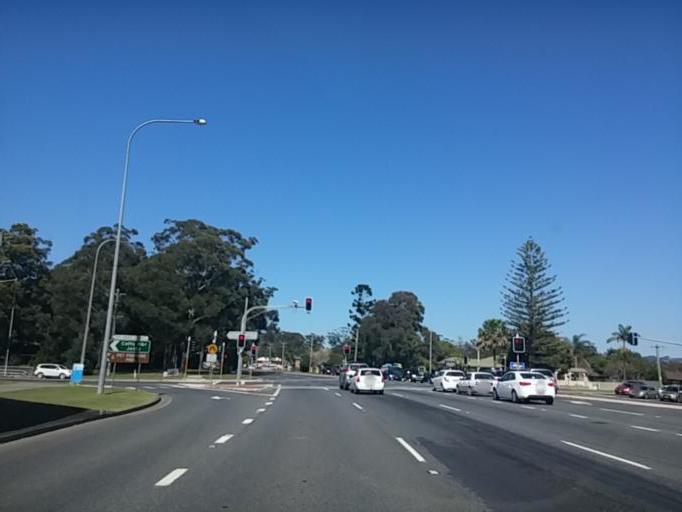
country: AU
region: New South Wales
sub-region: Coffs Harbour
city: Coffs Harbour
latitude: -30.2834
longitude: 153.1273
